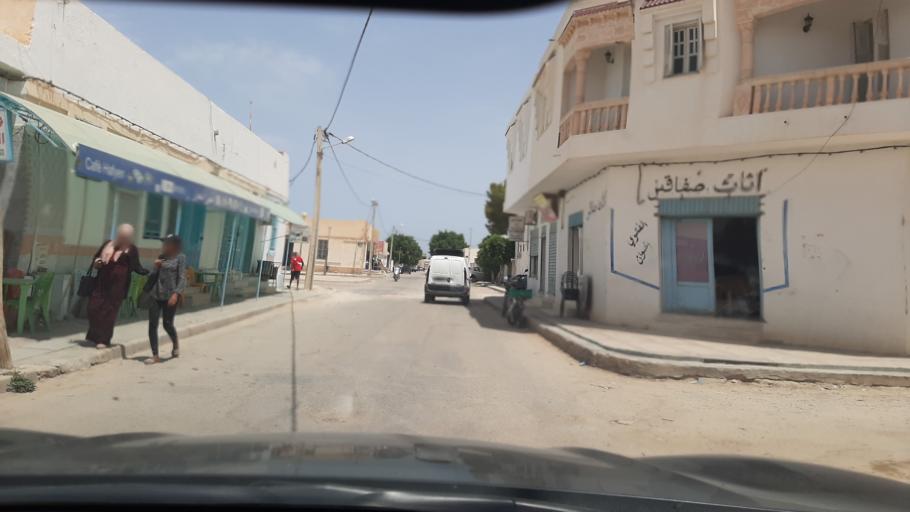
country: TN
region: Qabis
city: Matmata
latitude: 33.6167
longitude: 10.2893
